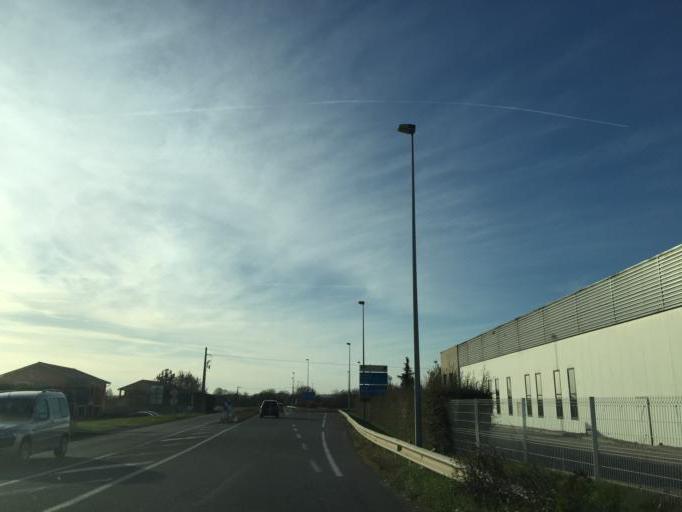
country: FR
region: Rhone-Alpes
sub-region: Departement de l'Ain
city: Chateau-Gaillard
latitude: 45.9762
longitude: 5.3143
